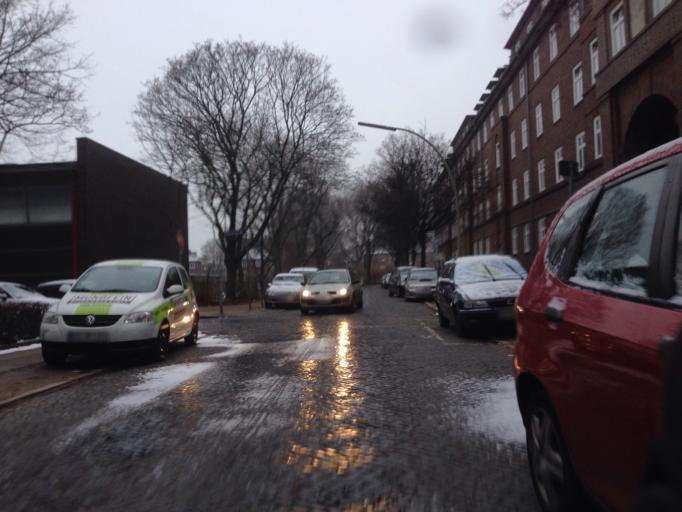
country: DE
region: Hamburg
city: Marienthal
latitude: 53.5819
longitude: 10.0607
